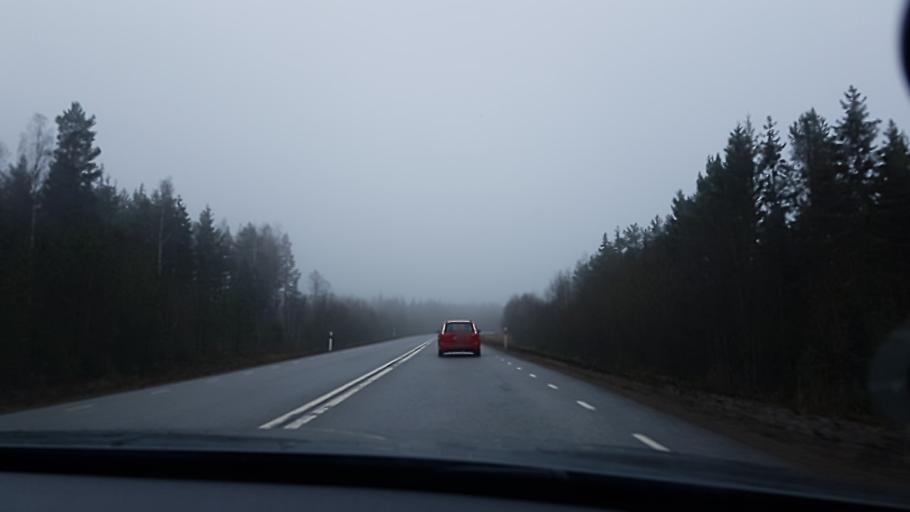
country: SE
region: Vaestra Goetaland
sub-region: Gullspangs Kommun
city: Gullspang
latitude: 58.8720
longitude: 14.0083
